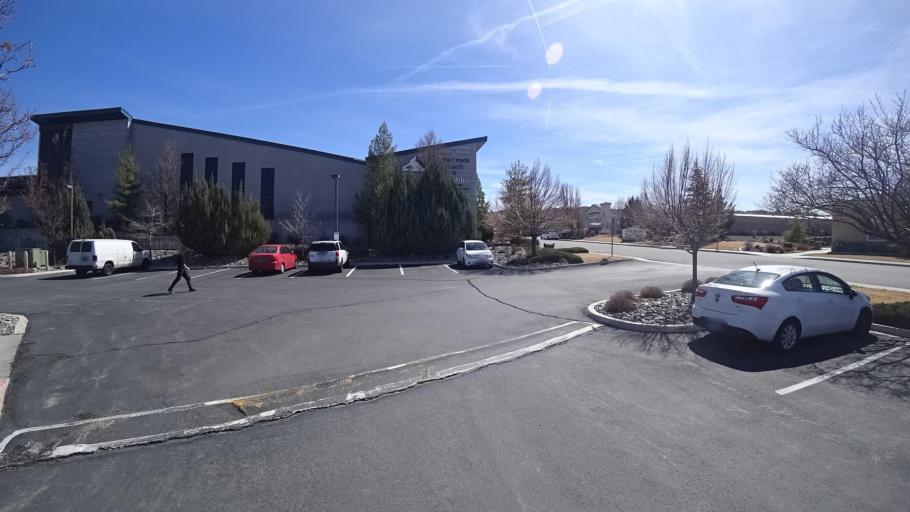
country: US
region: Nevada
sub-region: Washoe County
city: Sparks
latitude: 39.5803
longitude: -119.7171
